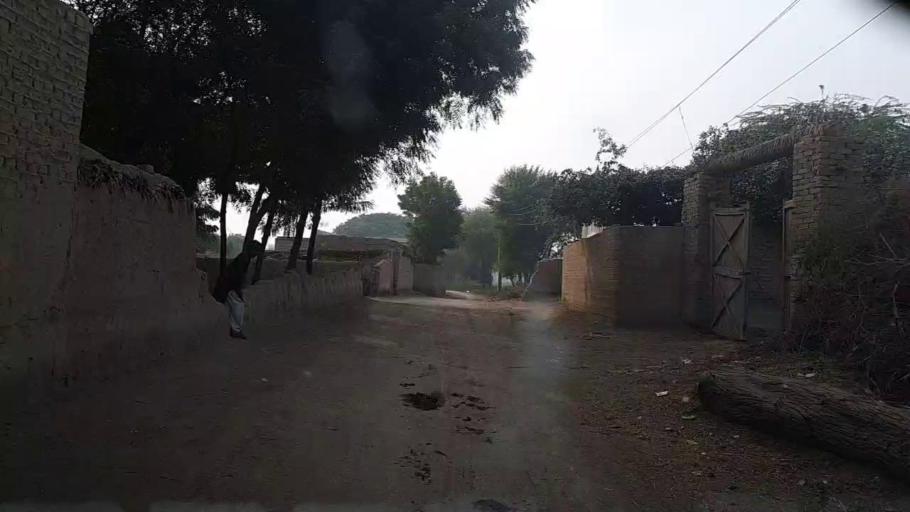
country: PK
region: Sindh
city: Bozdar
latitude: 27.1520
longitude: 68.6714
